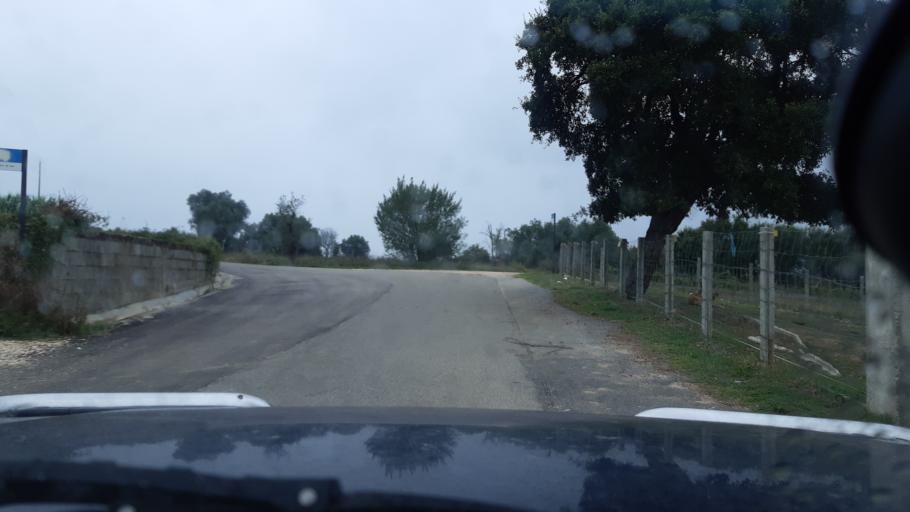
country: PT
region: Aveiro
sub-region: Oliveira do Bairro
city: Oliveira do Bairro
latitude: 40.5418
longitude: -8.5046
